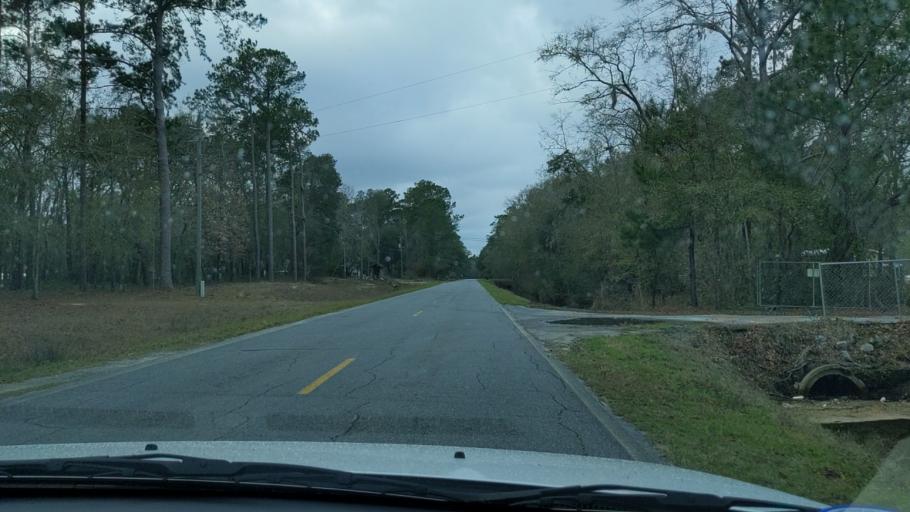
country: US
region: Georgia
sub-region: Chatham County
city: Georgetown
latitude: 32.0371
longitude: -81.3026
